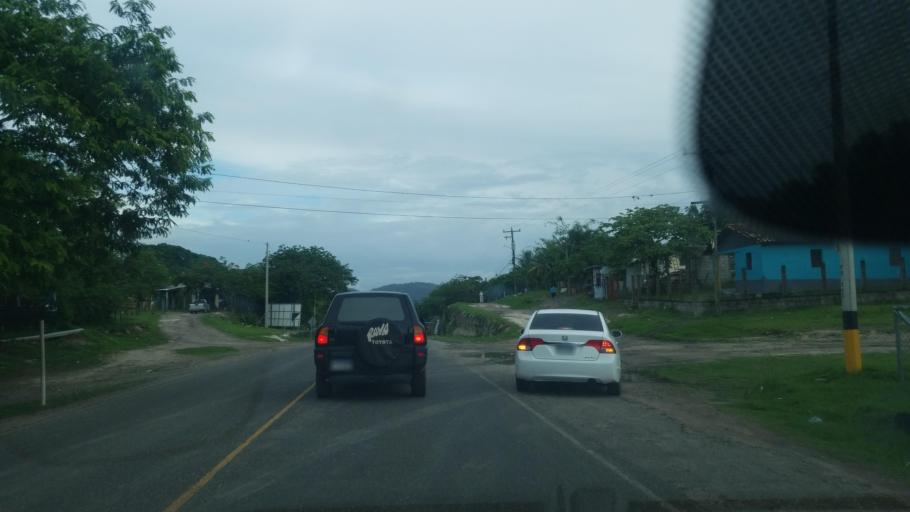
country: HN
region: Santa Barbara
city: Santa Barbara
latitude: 14.8985
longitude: -88.2524
